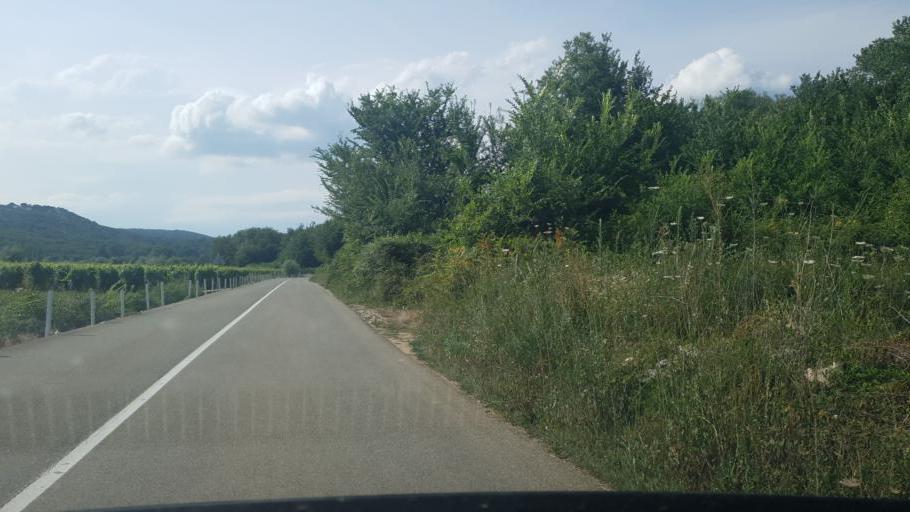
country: HR
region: Primorsko-Goranska
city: Punat
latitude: 45.0837
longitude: 14.6469
